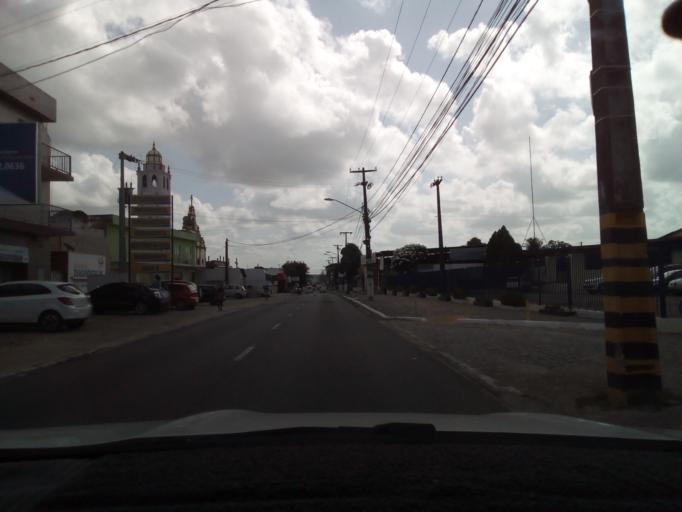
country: BR
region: Paraiba
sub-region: Bayeux
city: Bayeux
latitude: -7.1232
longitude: -34.9177
